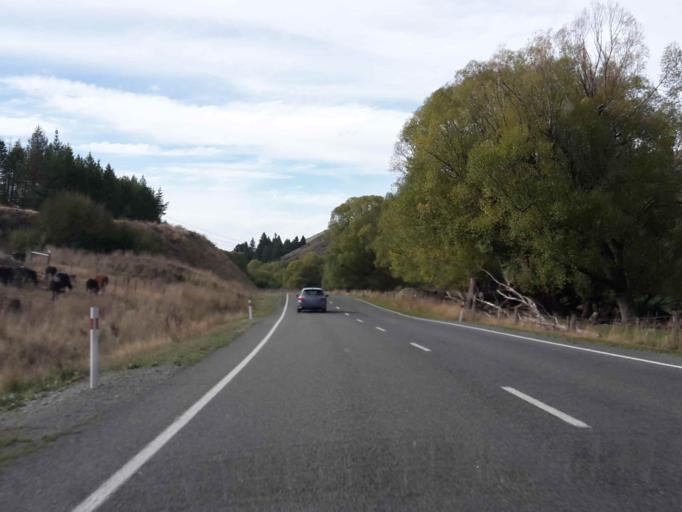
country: NZ
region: Canterbury
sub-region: Timaru District
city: Pleasant Point
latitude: -44.0695
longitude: 170.6691
